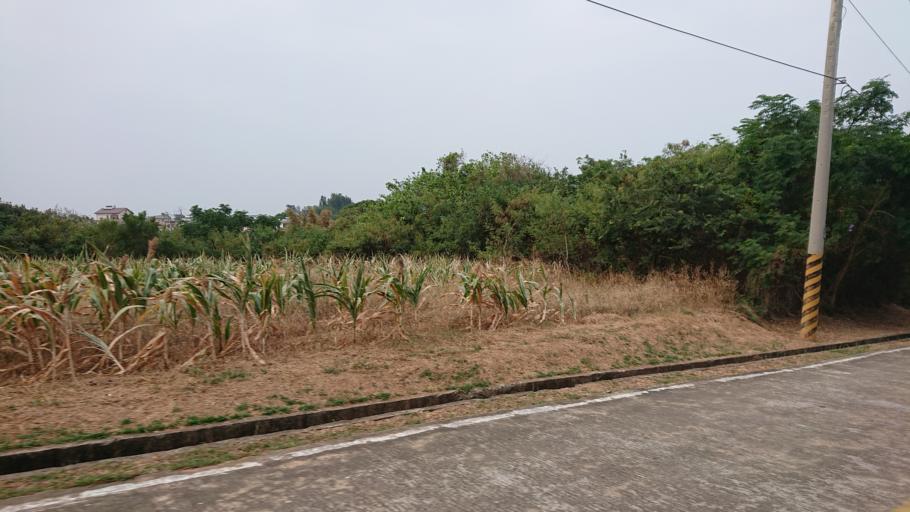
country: TW
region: Fukien
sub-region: Kinmen
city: Jincheng
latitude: 24.4444
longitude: 118.2535
